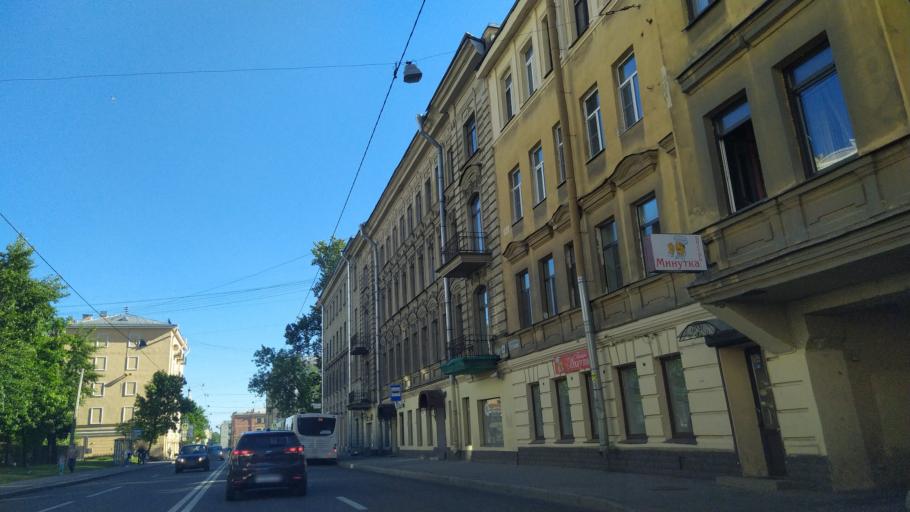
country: RU
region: Leningrad
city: Sampsonievskiy
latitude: 59.9718
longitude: 30.3403
